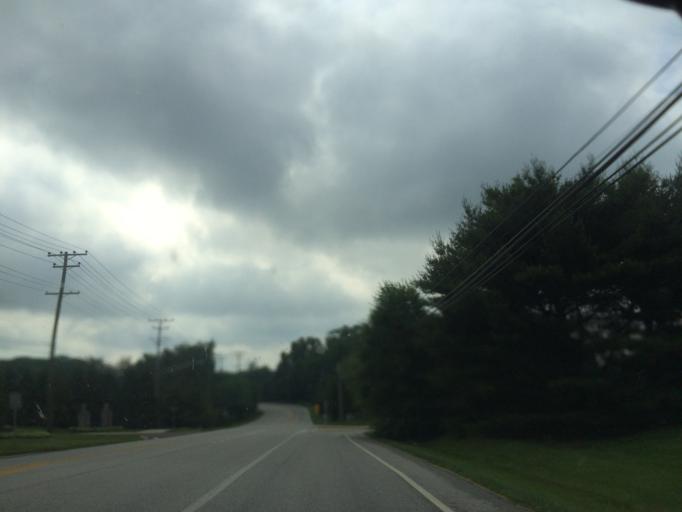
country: US
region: Maryland
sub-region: Howard County
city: Highland
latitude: 39.1885
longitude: -76.9229
